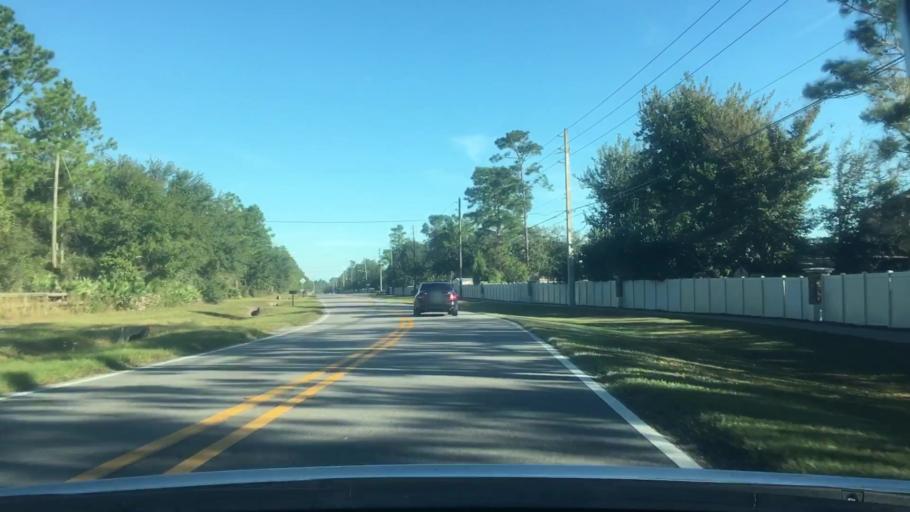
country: US
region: Florida
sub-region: Nassau County
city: Yulee
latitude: 30.4884
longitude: -81.5755
